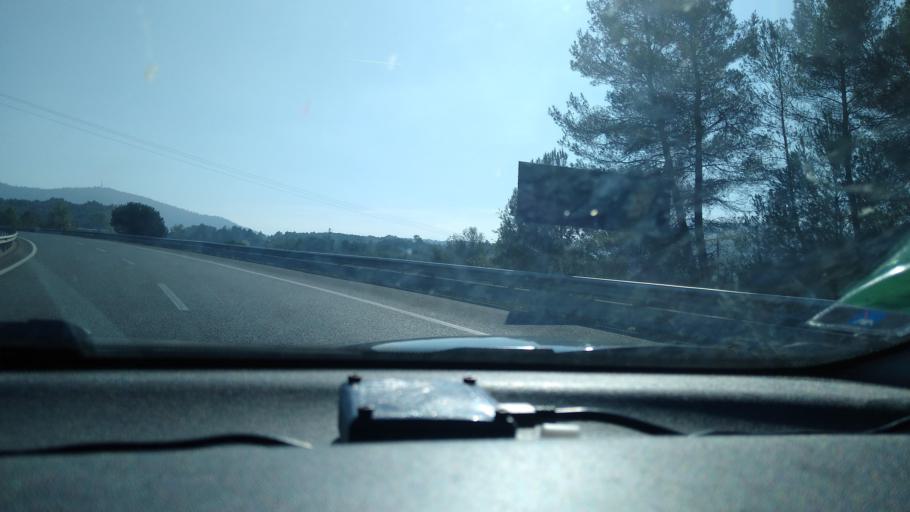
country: ES
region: Catalonia
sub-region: Provincia de Barcelona
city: Olesa de Montserrat
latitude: 41.5951
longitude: 1.9013
